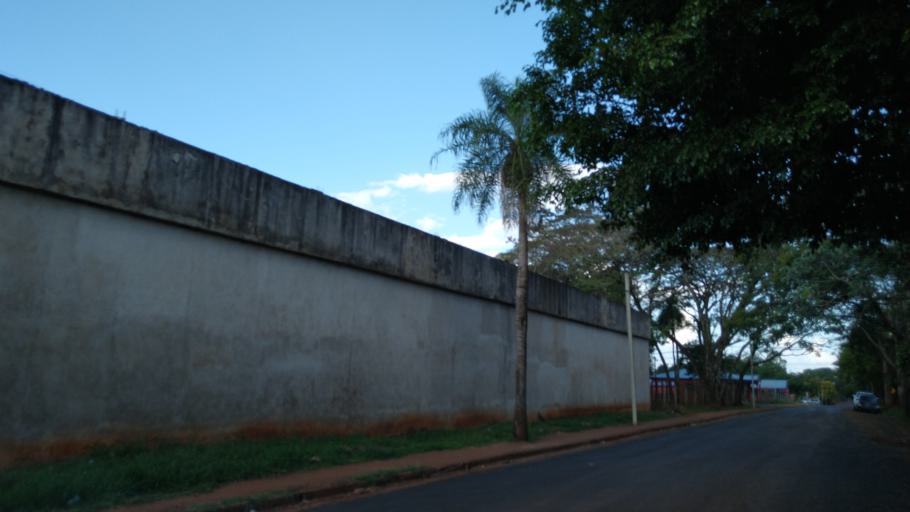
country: AR
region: Misiones
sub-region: Departamento de Capital
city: Posadas
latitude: -27.4027
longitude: -55.9274
